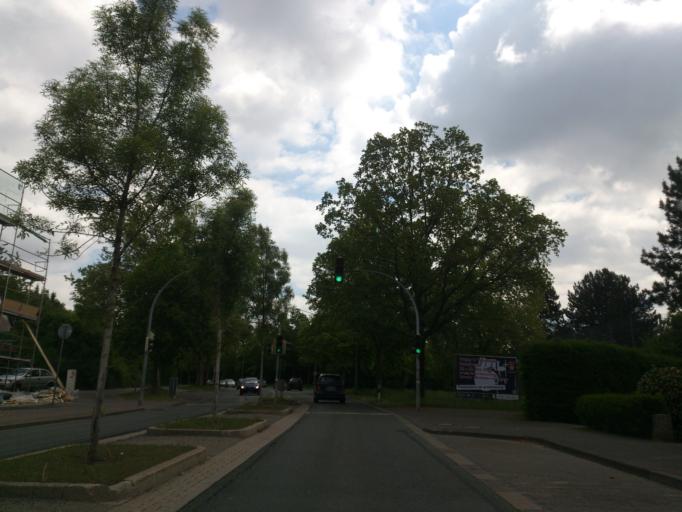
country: DE
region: North Rhine-Westphalia
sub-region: Regierungsbezirk Detmold
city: Paderborn
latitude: 51.7024
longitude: 8.7508
